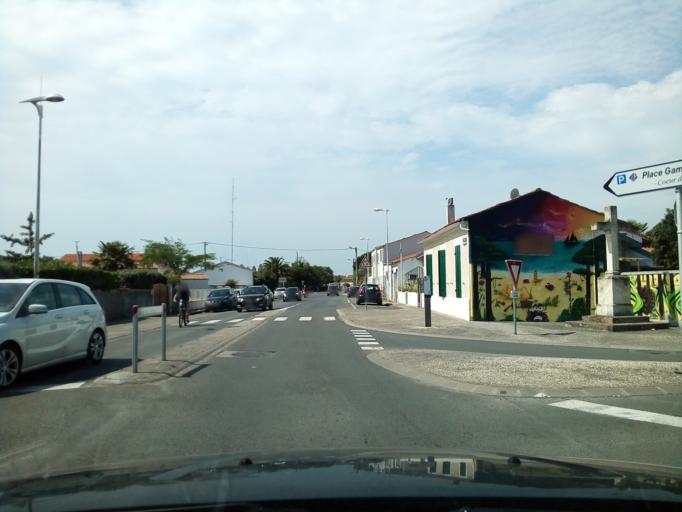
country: FR
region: Poitou-Charentes
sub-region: Departement de la Charente-Maritime
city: Dolus-d'Oleron
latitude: 45.9429
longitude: -1.3108
